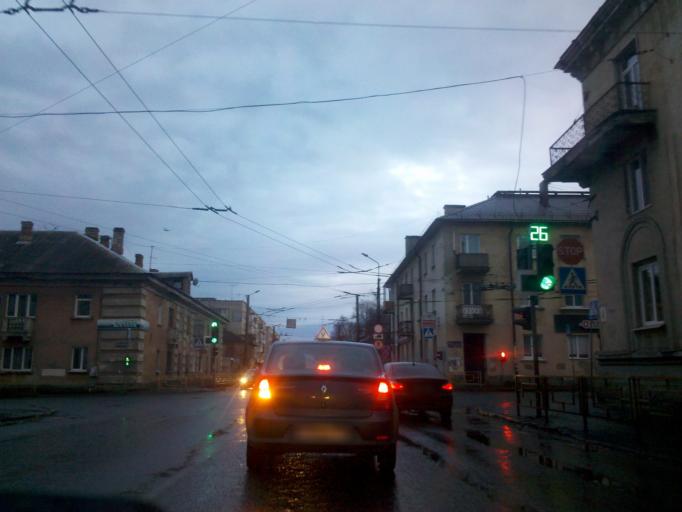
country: RU
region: Republic of Karelia
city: Petrozavodsk
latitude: 61.7841
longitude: 34.3921
